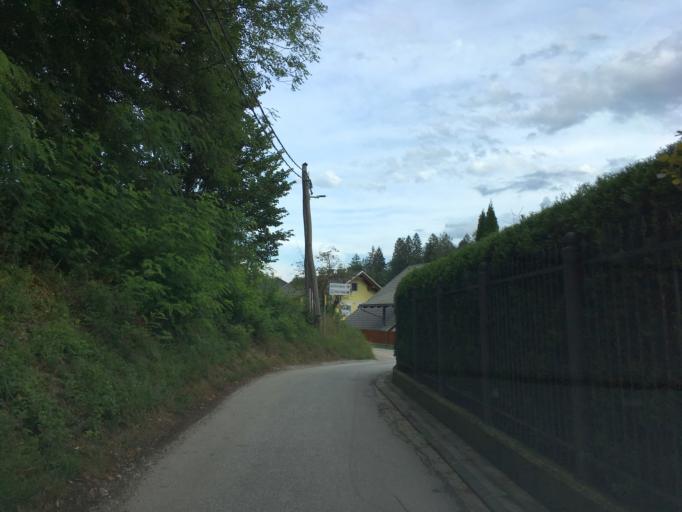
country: SI
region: Bled
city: Bled
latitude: 46.3581
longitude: 14.0982
